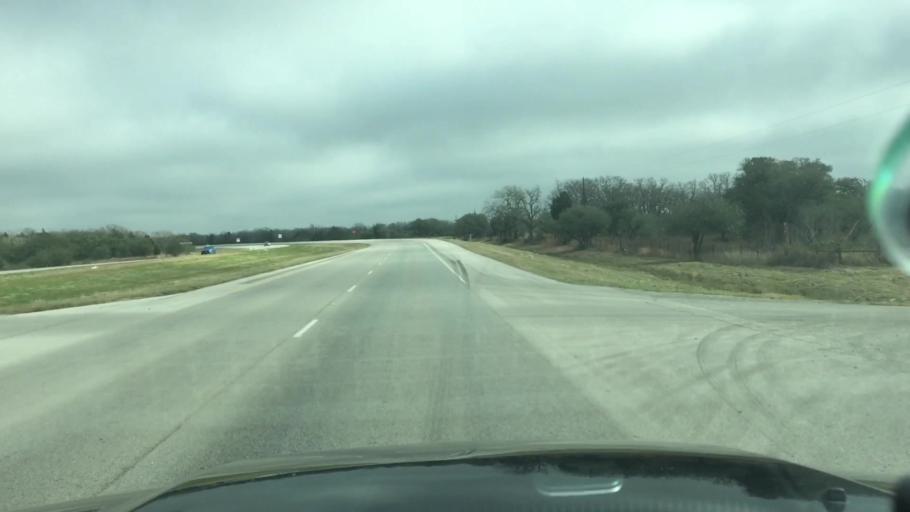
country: US
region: Texas
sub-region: Lee County
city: Giddings
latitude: 30.1416
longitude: -96.7686
